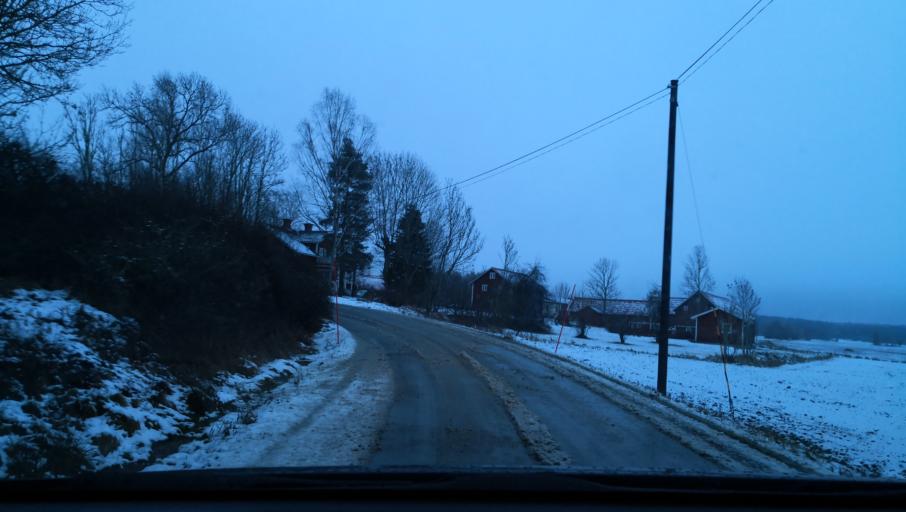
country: SE
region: Vaestmanland
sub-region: Kungsors Kommun
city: Kungsoer
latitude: 59.3946
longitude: 16.2101
